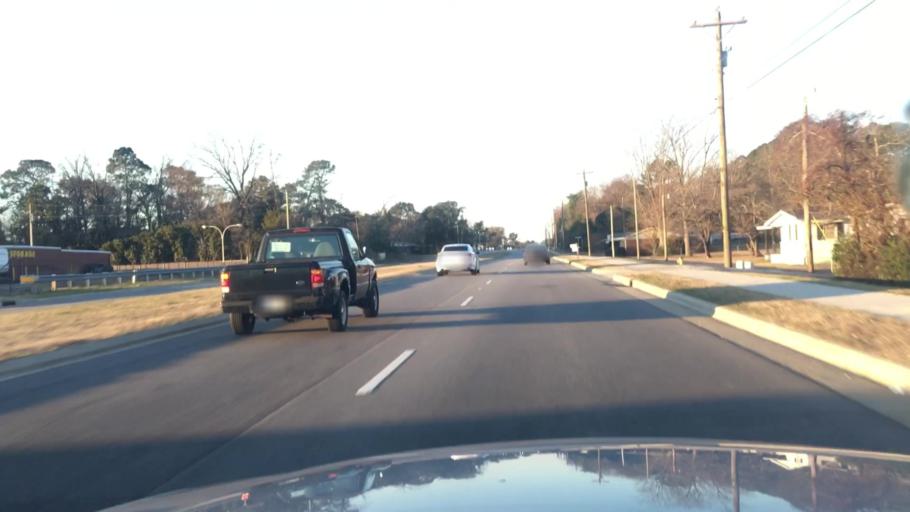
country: US
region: North Carolina
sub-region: Cumberland County
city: Hope Mills
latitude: 35.0065
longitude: -78.9208
